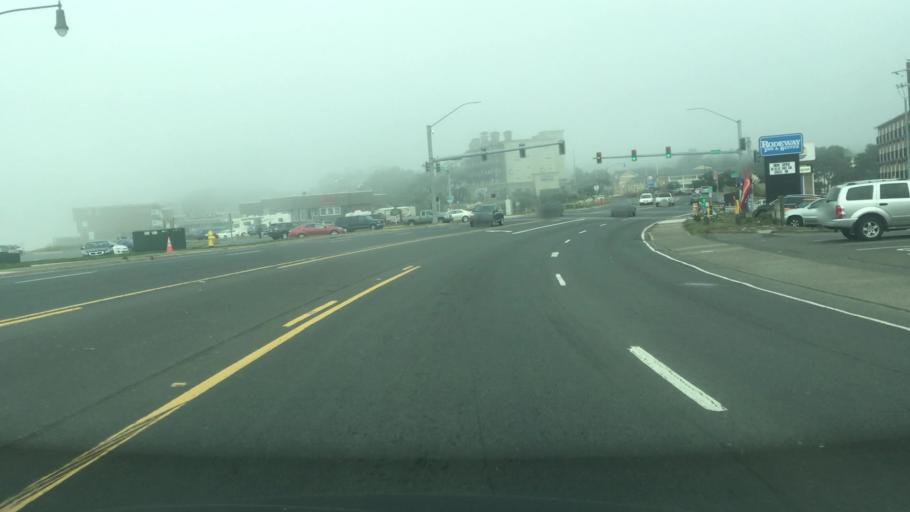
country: US
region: Oregon
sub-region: Lincoln County
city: Lincoln City
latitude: 44.9665
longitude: -124.0175
